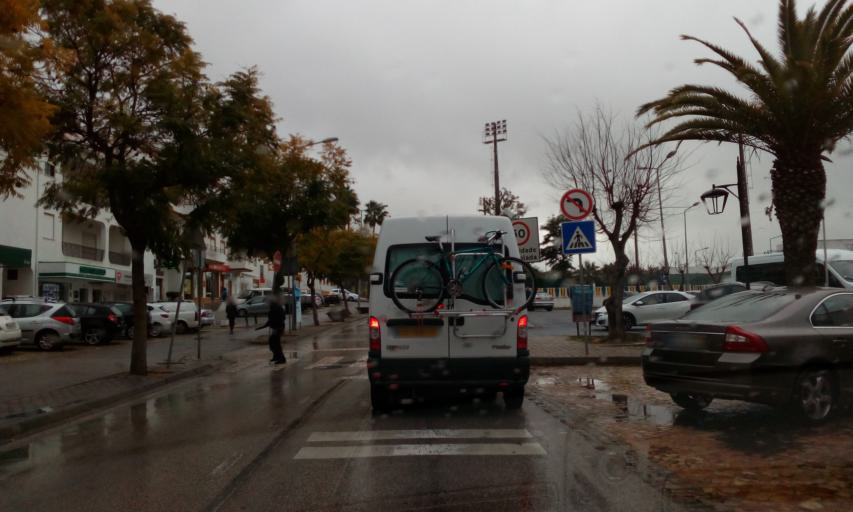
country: PT
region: Faro
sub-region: Albufeira
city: Guia
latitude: 37.1266
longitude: -8.3012
